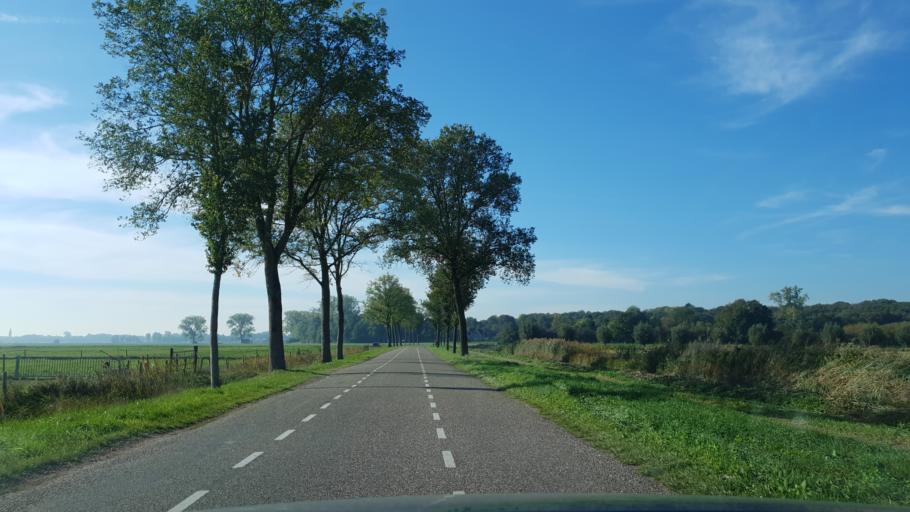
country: NL
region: Gelderland
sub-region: Gemeente Wijchen
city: Bergharen
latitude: 51.8581
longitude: 5.6831
